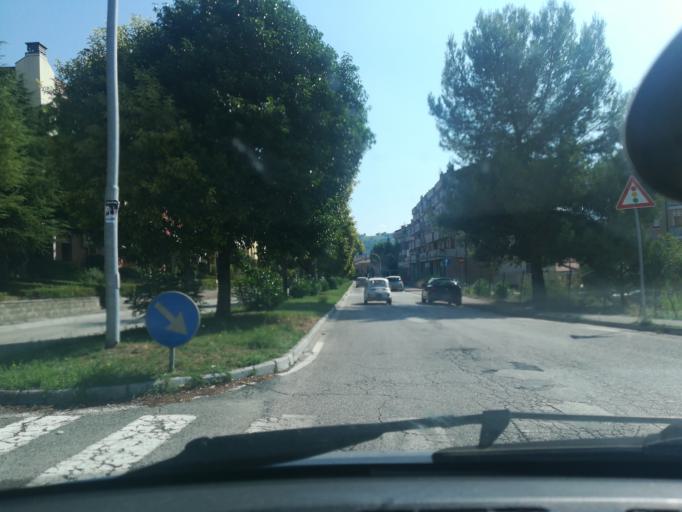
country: IT
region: The Marches
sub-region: Provincia di Macerata
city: Tolentino
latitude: 43.2142
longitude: 13.2996
